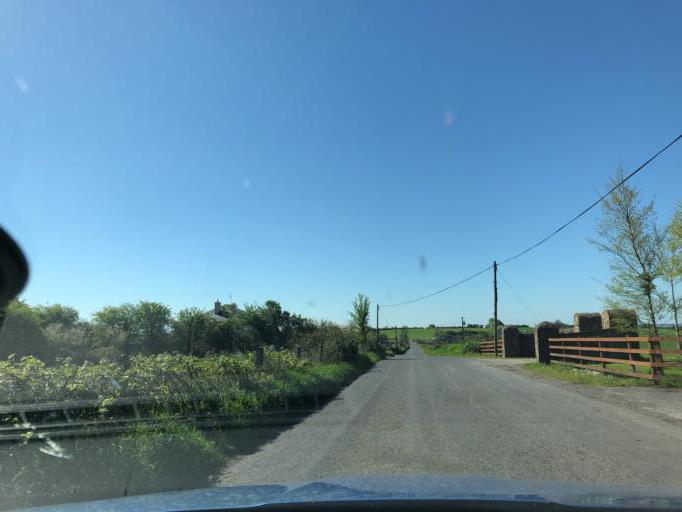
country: IE
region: Connaught
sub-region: County Galway
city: Portumna
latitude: 53.1611
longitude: -8.2943
